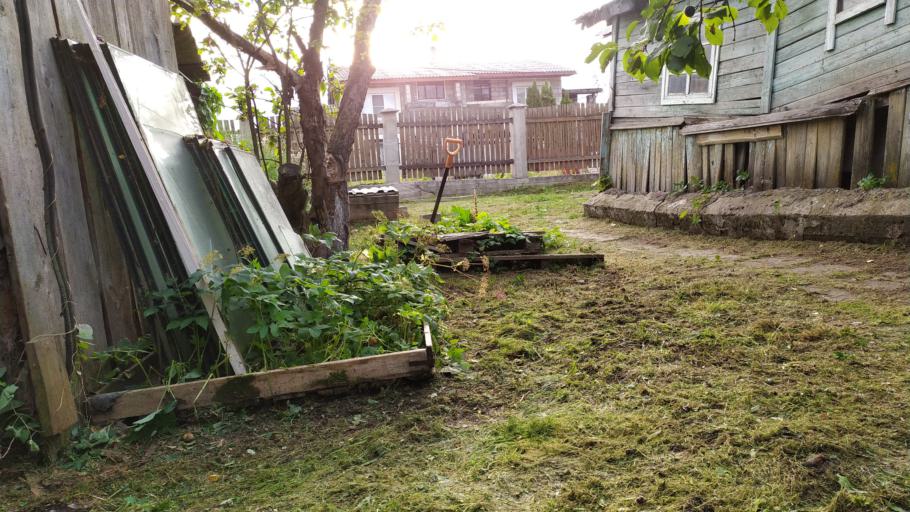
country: RU
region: Leningrad
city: Kirovsk
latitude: 59.8786
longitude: 30.9982
